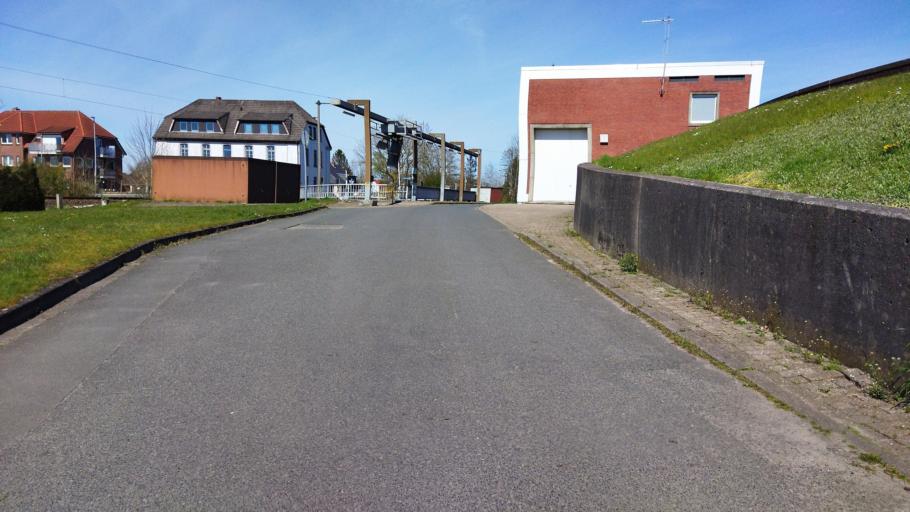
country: DE
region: Lower Saxony
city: Nordenham
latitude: 53.4674
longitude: 8.4770
